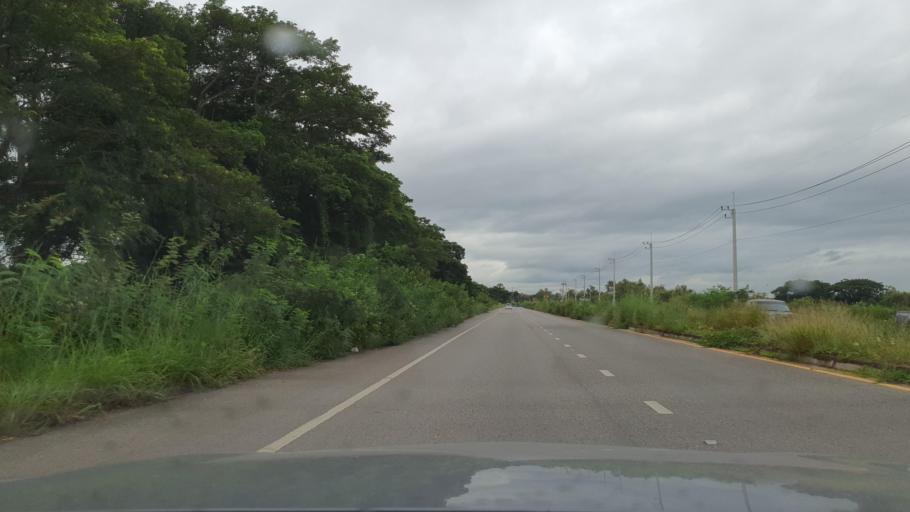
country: TH
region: Lamphun
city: Lamphun
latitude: 18.6056
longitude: 99.0117
